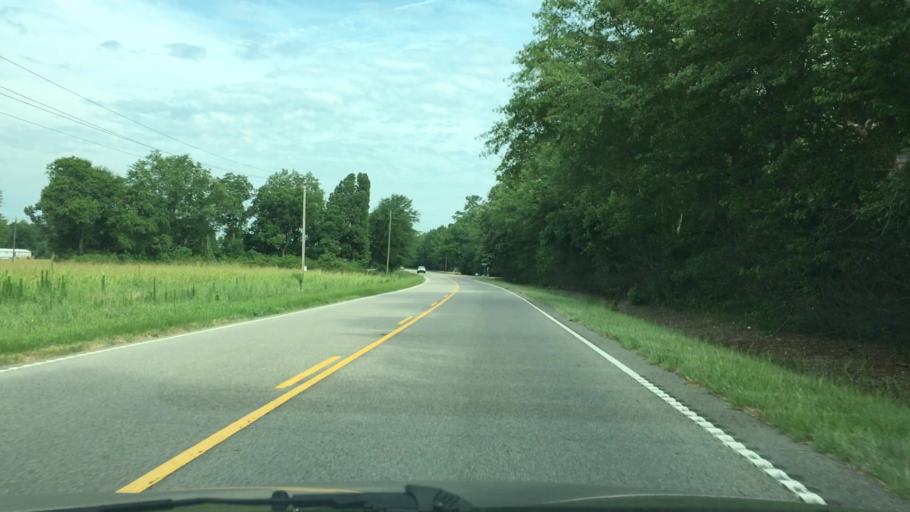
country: US
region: South Carolina
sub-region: Barnwell County
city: Williston
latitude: 33.6664
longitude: -81.3977
